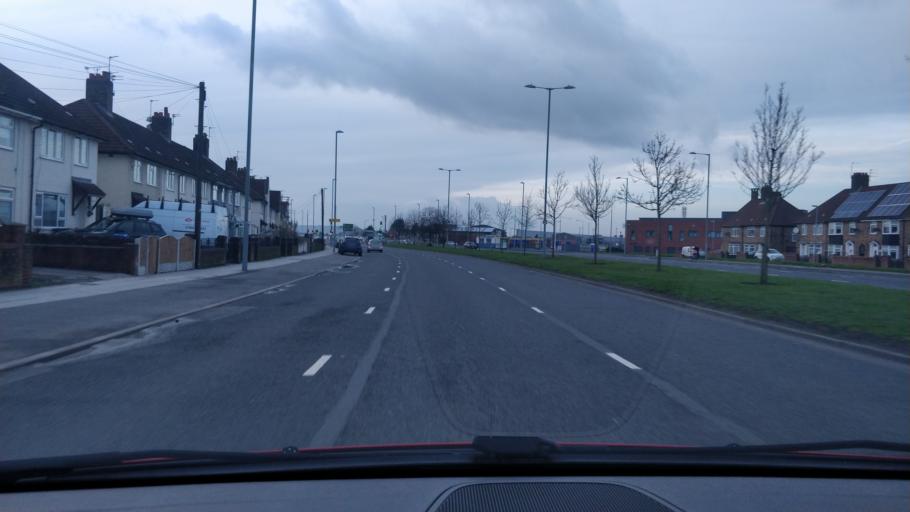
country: GB
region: England
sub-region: Knowsley
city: Huyton
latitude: 53.4210
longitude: -2.8567
